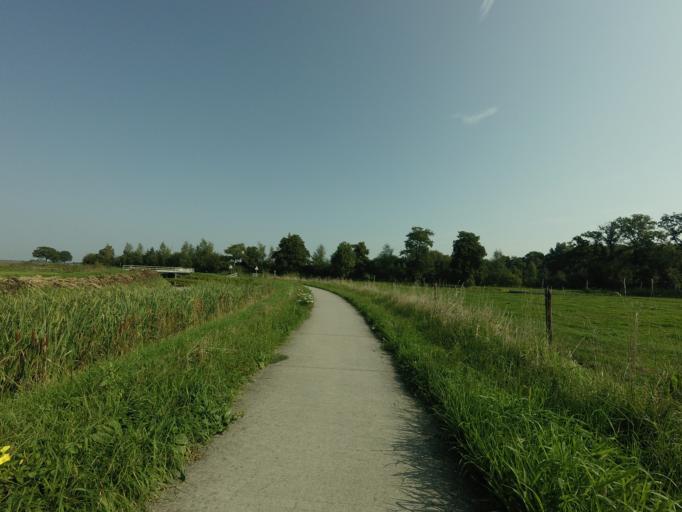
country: NL
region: Groningen
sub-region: Gemeente Groningen
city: Groningen
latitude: 53.1600
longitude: 6.5421
